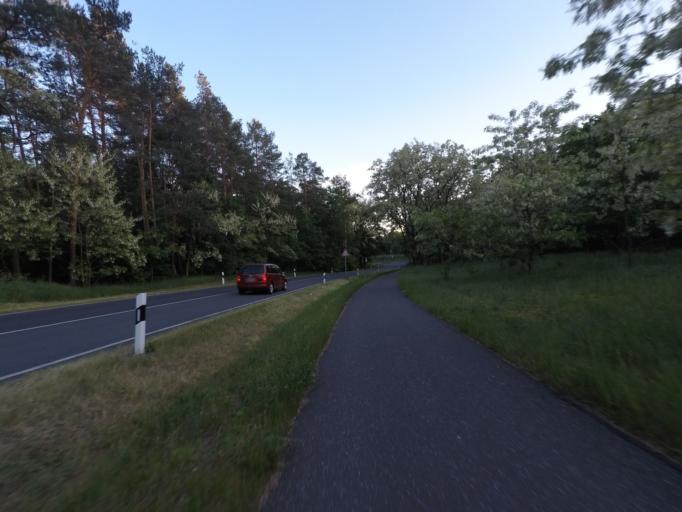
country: DE
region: Brandenburg
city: Marienwerder
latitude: 52.8582
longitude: 13.6501
